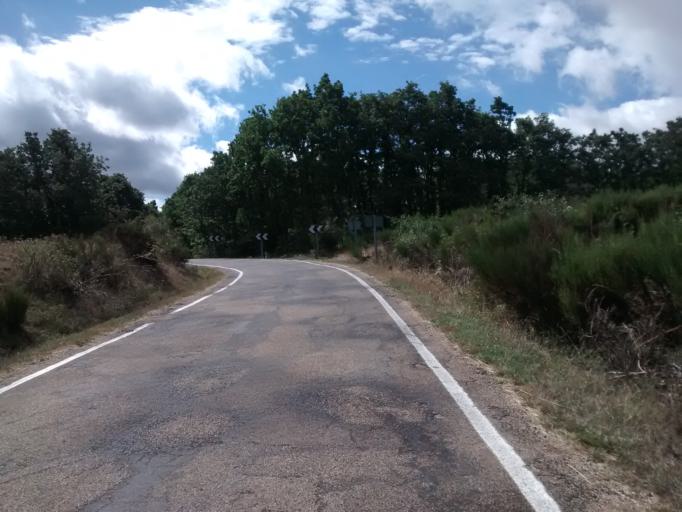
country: ES
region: Castille and Leon
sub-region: Provincia de Palencia
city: Polentinos
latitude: 42.9340
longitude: -4.4666
